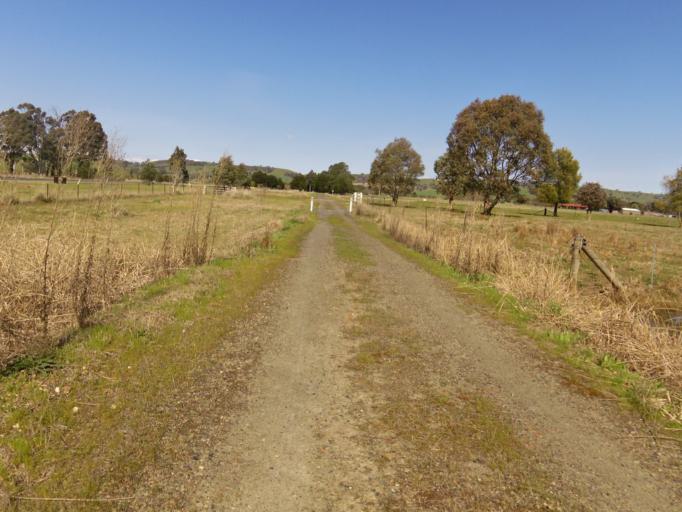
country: AU
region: Victoria
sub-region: Murrindindi
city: Alexandra
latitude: -37.0050
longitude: 145.7492
